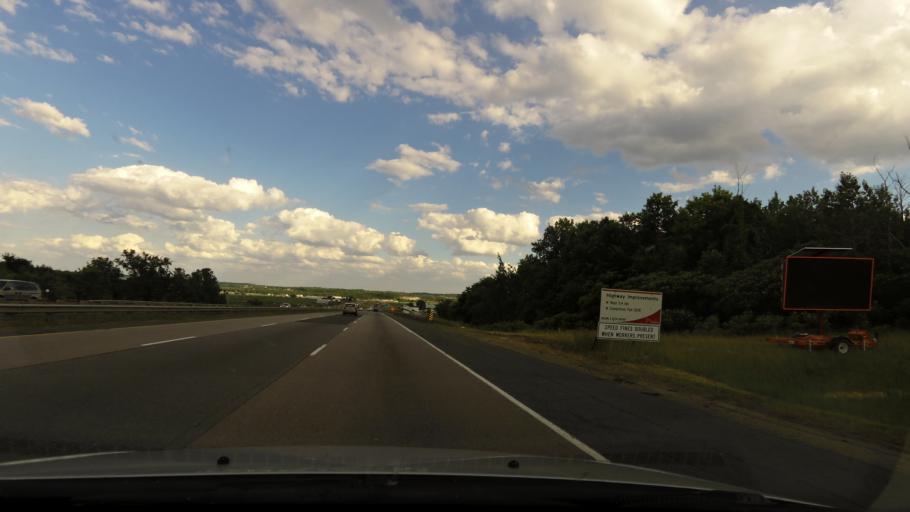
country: CA
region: Ontario
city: Bradford West Gwillimbury
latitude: 44.0548
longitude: -79.6116
